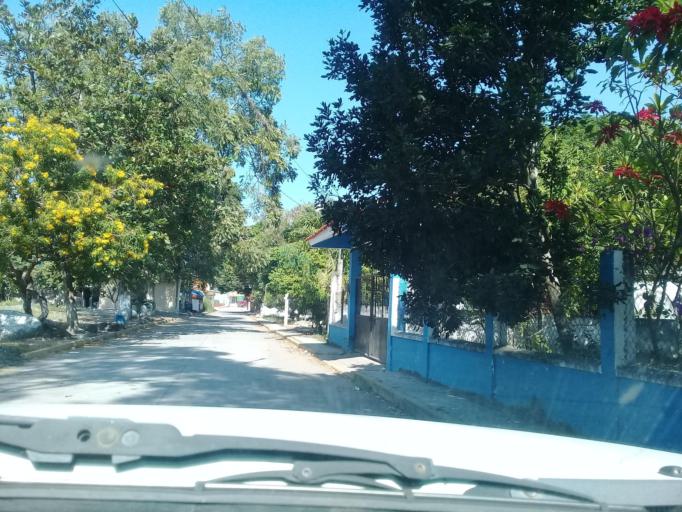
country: MX
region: Veracruz
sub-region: Emiliano Zapata
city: Plan del Rio
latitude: 19.4148
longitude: -96.6180
